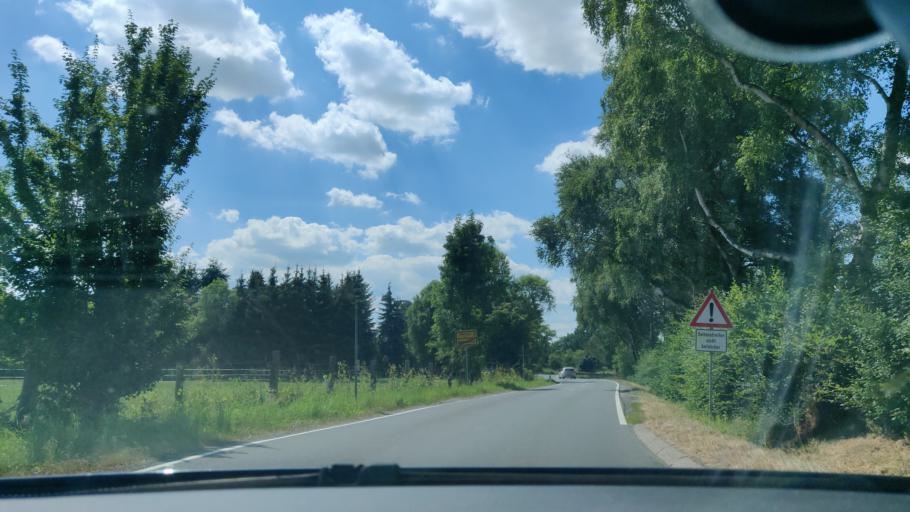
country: DE
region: Hesse
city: Gudensberg
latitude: 51.1581
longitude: 9.3534
